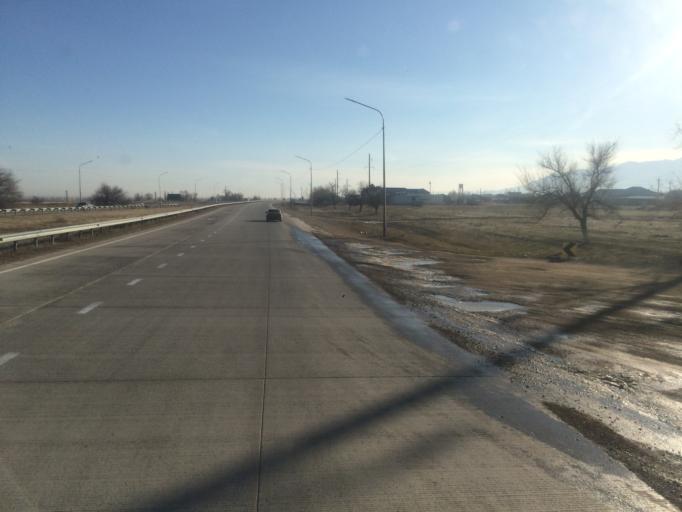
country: KZ
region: Zhambyl
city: Sarykemer
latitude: 43.0091
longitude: 71.7930
